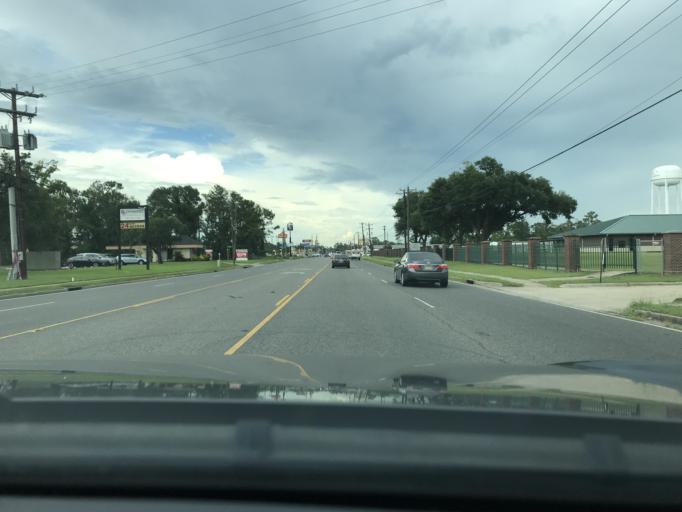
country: US
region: Louisiana
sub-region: Calcasieu Parish
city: Moss Bluff
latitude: 30.3006
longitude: -93.2048
